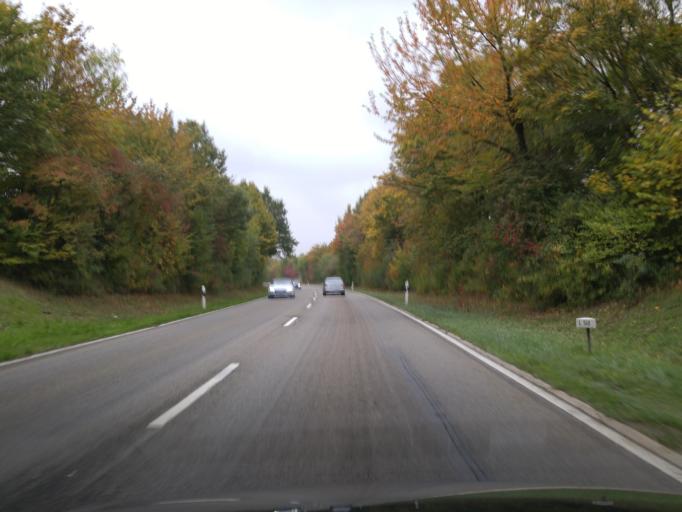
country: DE
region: Baden-Wuerttemberg
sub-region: Regierungsbezirk Stuttgart
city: Bad Rappenau
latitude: 49.2242
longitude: 9.0779
